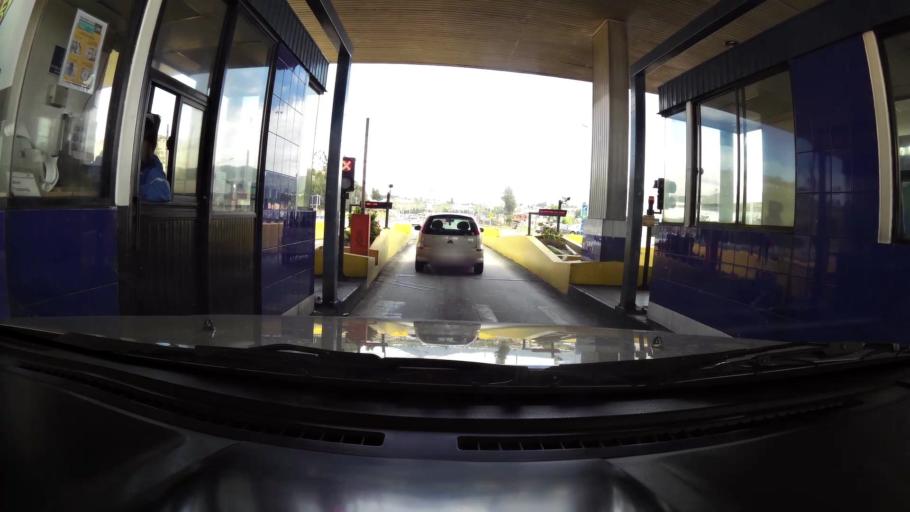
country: EC
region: Cotopaxi
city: San Miguel de Salcedo
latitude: -1.0720
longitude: -78.5955
